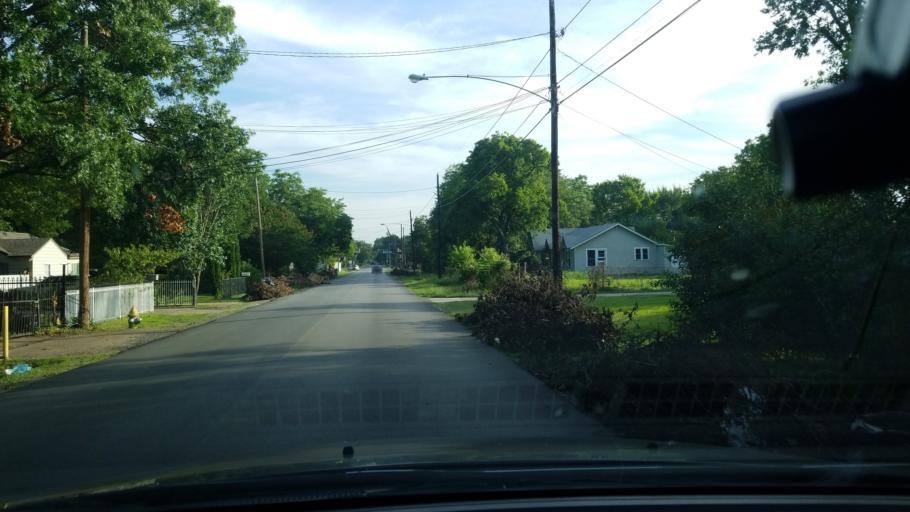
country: US
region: Texas
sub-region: Dallas County
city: Balch Springs
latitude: 32.7322
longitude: -96.6884
